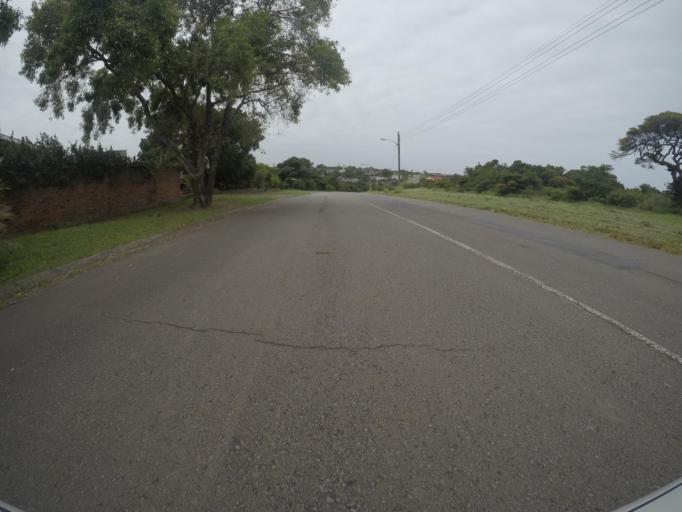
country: ZA
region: Eastern Cape
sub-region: Buffalo City Metropolitan Municipality
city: East London
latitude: -32.9752
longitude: 27.9442
